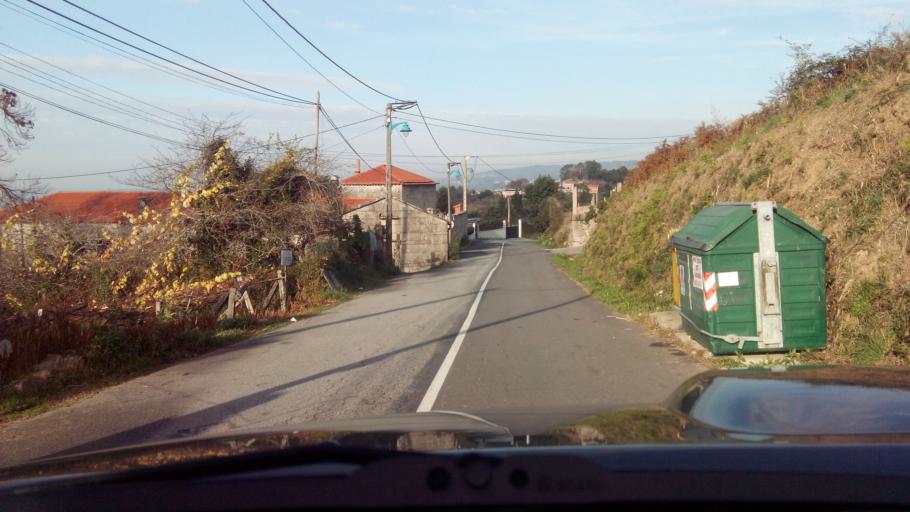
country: ES
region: Galicia
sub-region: Provincia de Pontevedra
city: Marin
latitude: 42.3653
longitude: -8.7184
